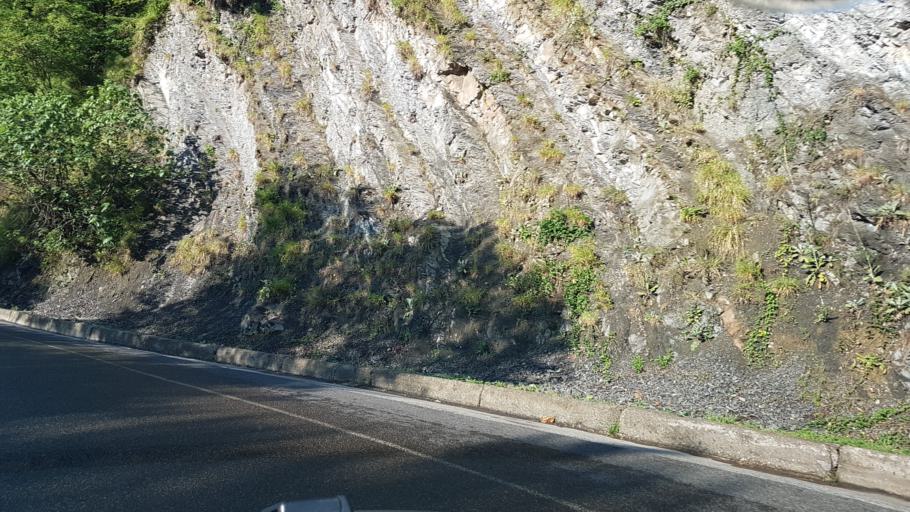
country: RU
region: Krasnodarskiy
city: Vardane
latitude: 43.8038
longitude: 39.4551
